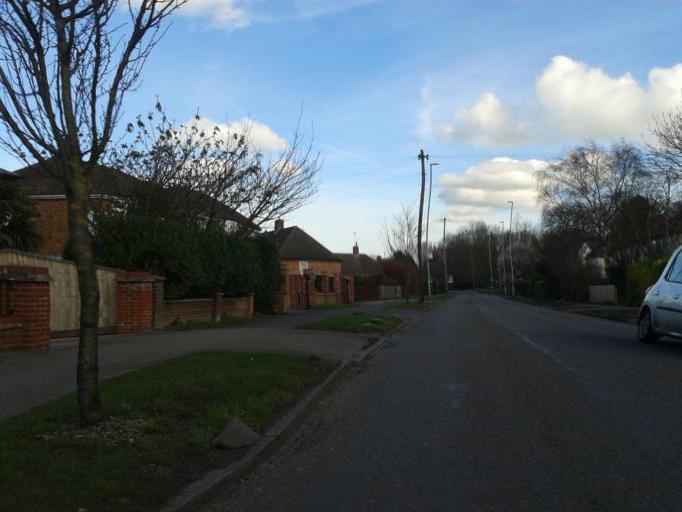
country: GB
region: England
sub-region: Cambridgeshire
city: Fulbourn
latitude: 52.1825
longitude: 0.1676
